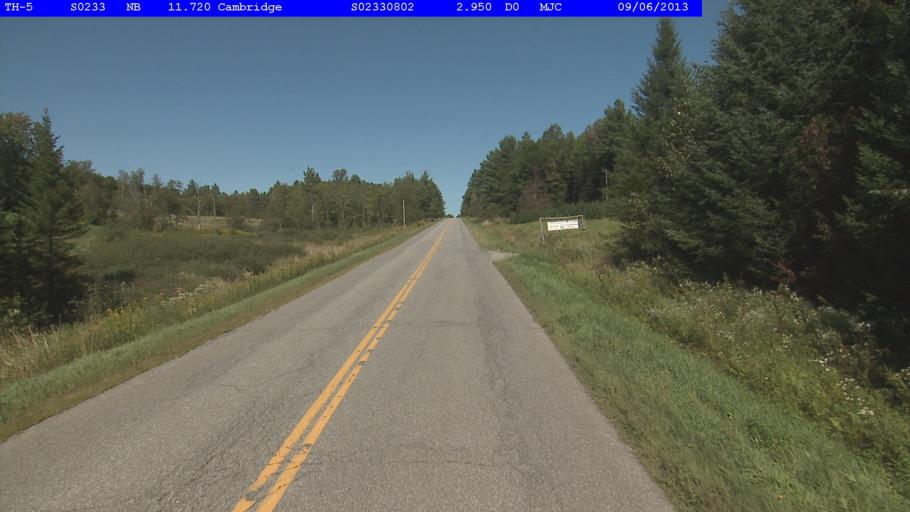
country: US
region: Vermont
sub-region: Lamoille County
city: Johnson
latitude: 44.6233
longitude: -72.8531
